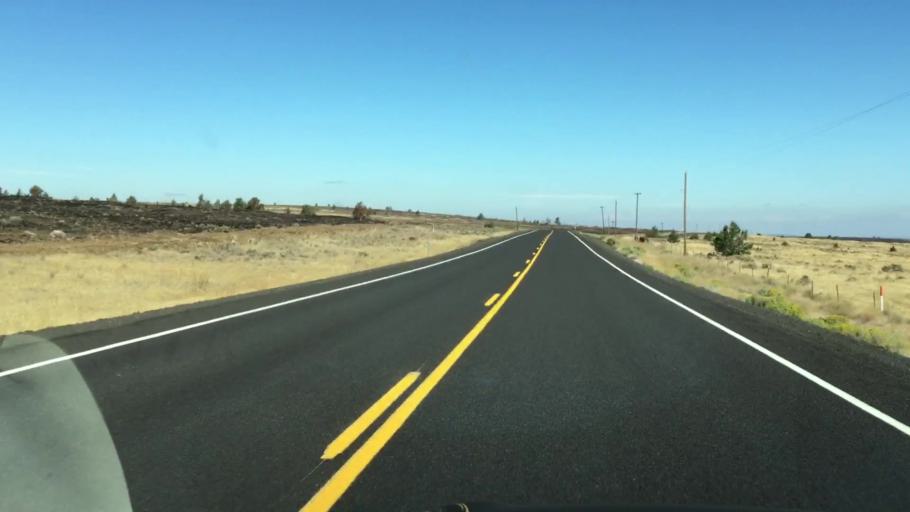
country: US
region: Oregon
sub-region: Jefferson County
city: Warm Springs
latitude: 44.9873
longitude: -120.9935
